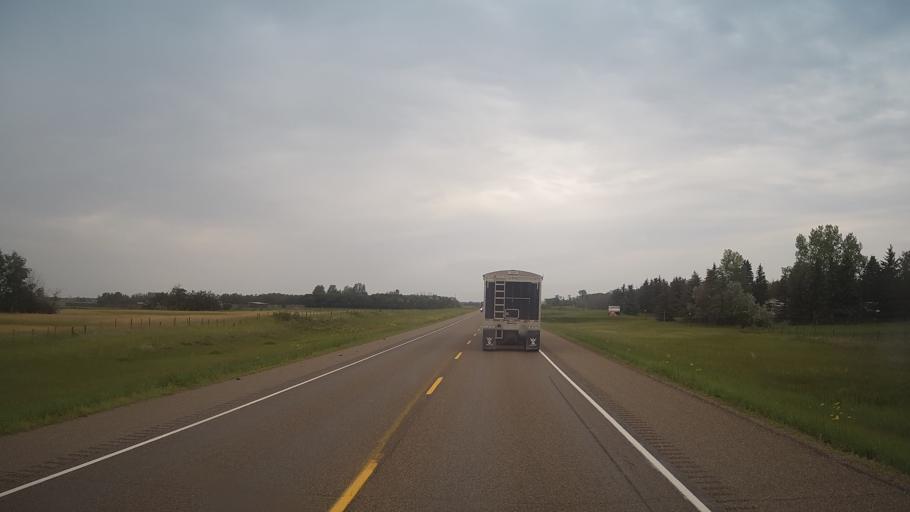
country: CA
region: Saskatchewan
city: Langham
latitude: 52.1294
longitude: -107.0596
